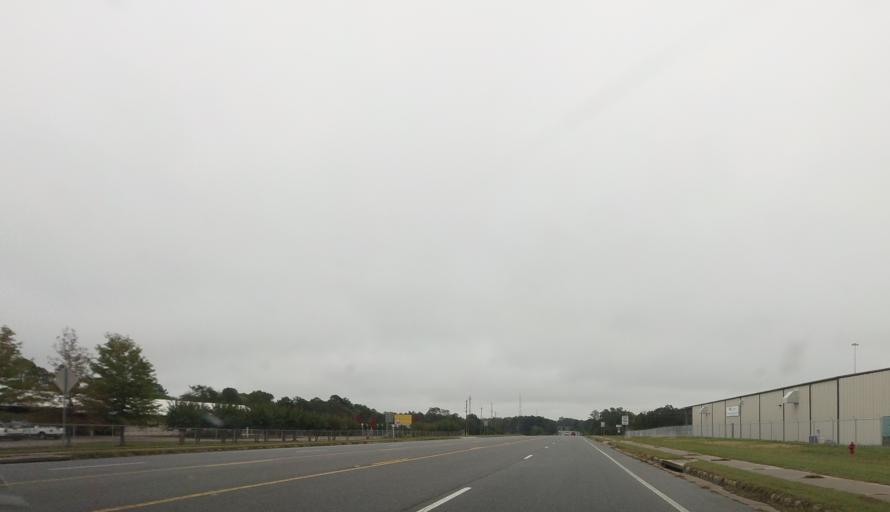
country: US
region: Georgia
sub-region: Taylor County
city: Reynolds
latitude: 32.5608
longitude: -84.1080
